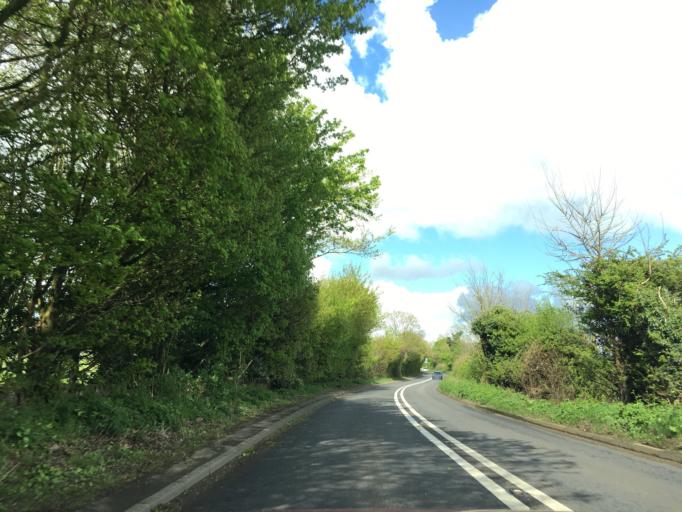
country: GB
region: England
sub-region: Gloucestershire
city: Tetbury
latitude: 51.6238
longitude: -2.1736
